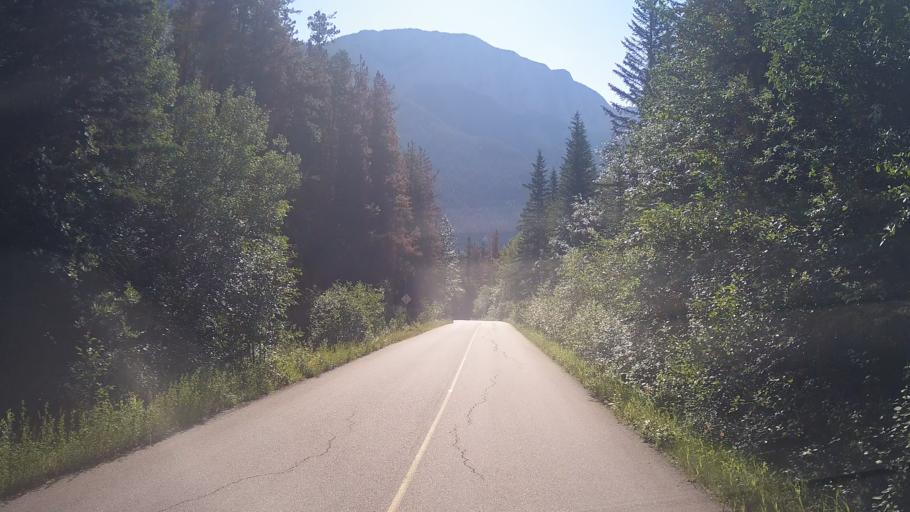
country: CA
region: Alberta
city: Hinton
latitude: 53.1772
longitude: -117.8435
